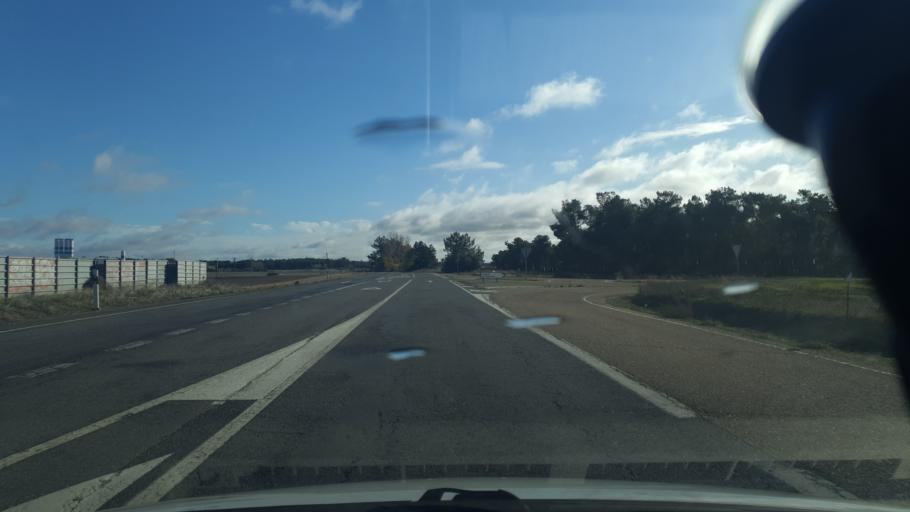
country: ES
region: Castille and Leon
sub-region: Provincia de Segovia
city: Martin Munoz de la Dehesa
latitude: 41.0462
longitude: -4.6836
